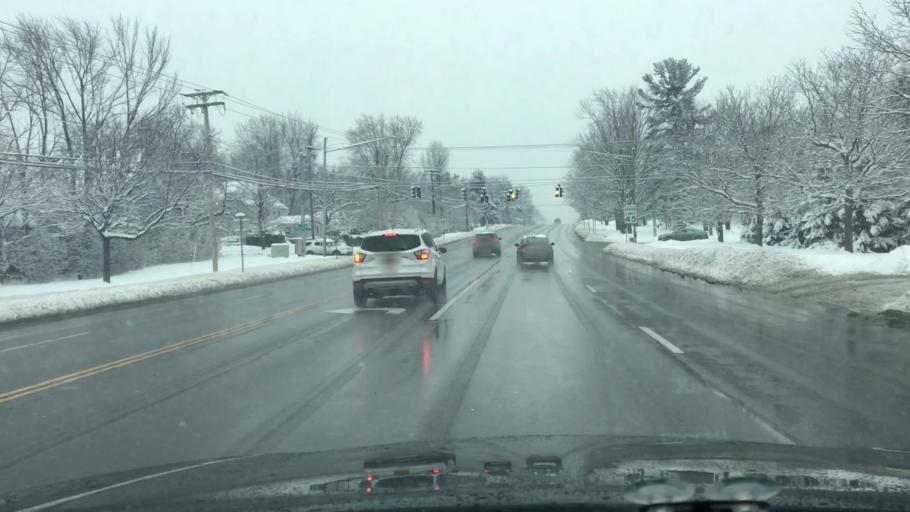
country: US
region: New York
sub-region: Erie County
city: Orchard Park
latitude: 42.8120
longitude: -78.7520
